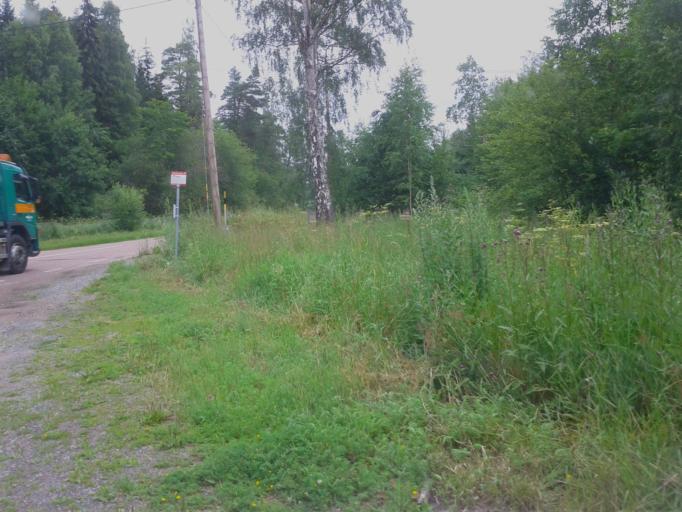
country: SE
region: Dalarna
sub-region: Smedjebackens Kommun
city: Smedjebacken
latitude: 60.3083
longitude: 15.3726
